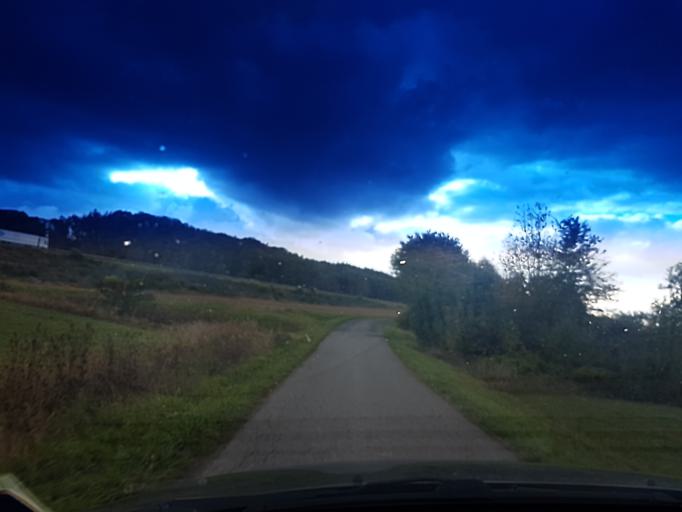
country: DE
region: Bavaria
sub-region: Regierungsbezirk Mittelfranken
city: Burghaslach
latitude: 49.7634
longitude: 10.5524
